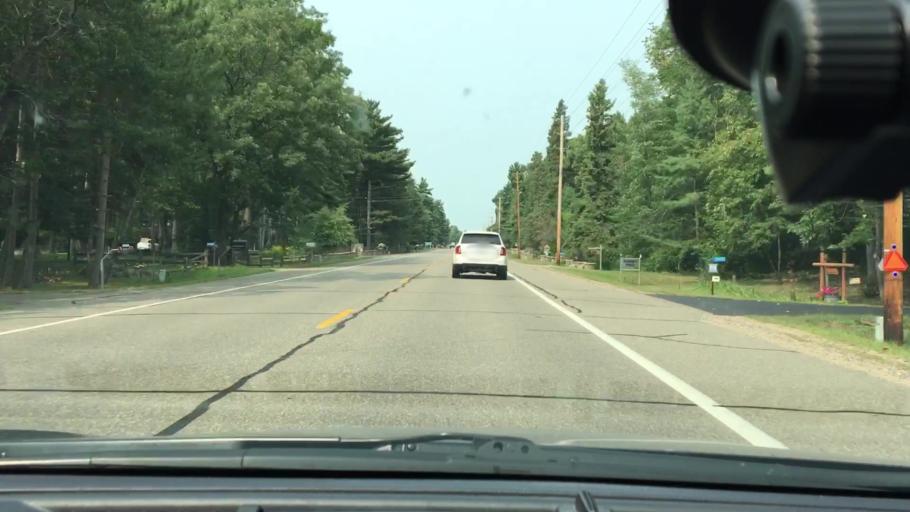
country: US
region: Minnesota
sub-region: Crow Wing County
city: Cross Lake
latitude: 46.5875
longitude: -94.1315
